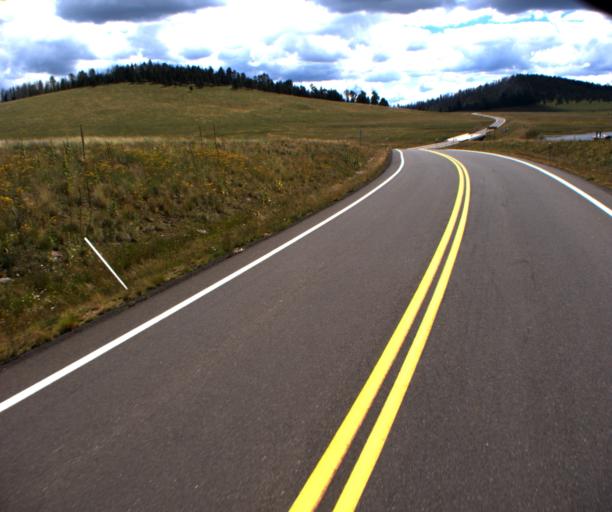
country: US
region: Arizona
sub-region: Apache County
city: Eagar
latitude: 33.9189
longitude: -109.4284
